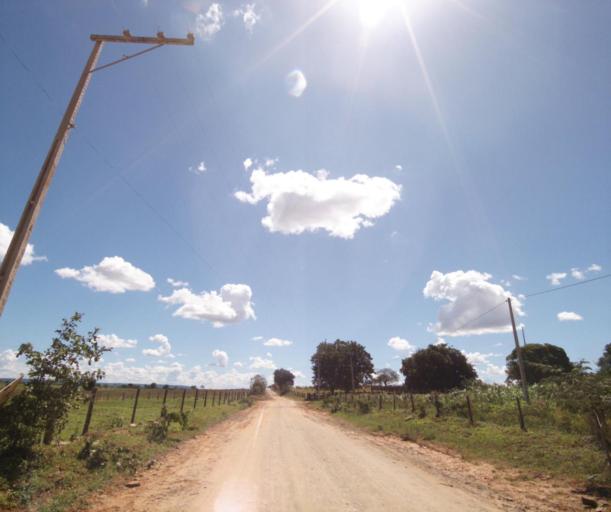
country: BR
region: Bahia
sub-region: Carinhanha
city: Carinhanha
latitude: -14.2173
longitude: -44.2874
